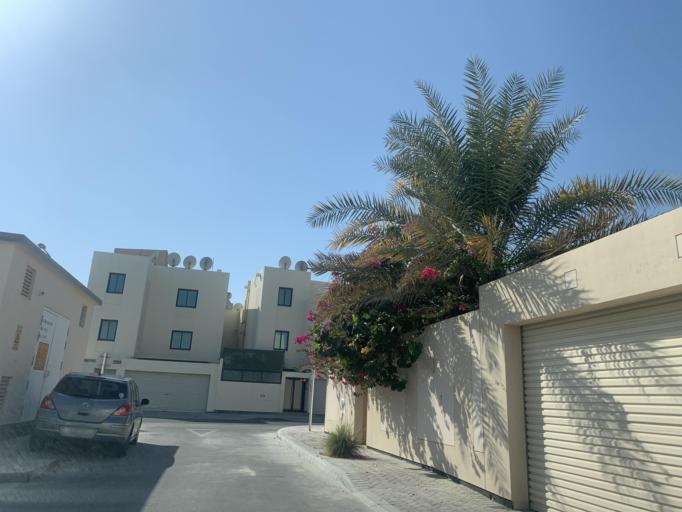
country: BH
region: Central Governorate
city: Madinat Hamad
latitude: 26.1202
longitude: 50.4817
